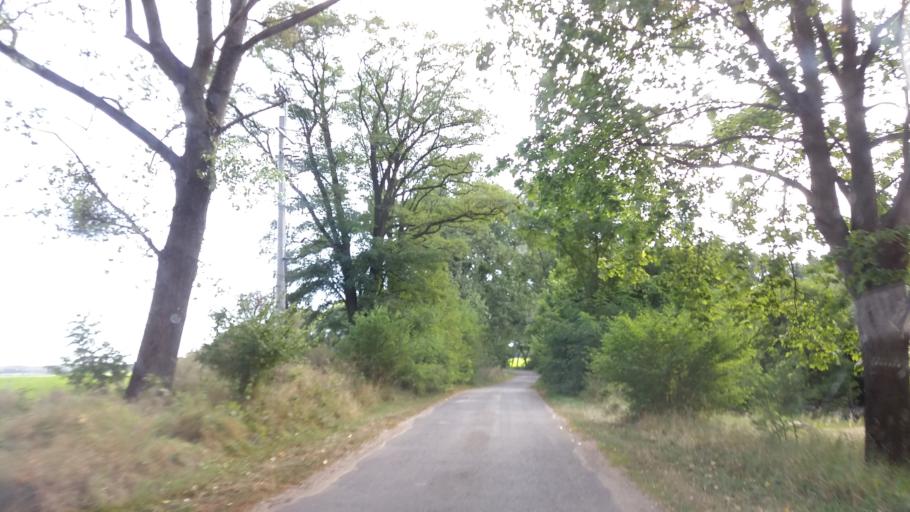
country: PL
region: West Pomeranian Voivodeship
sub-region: Powiat stargardzki
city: Suchan
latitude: 53.2301
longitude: 15.3599
